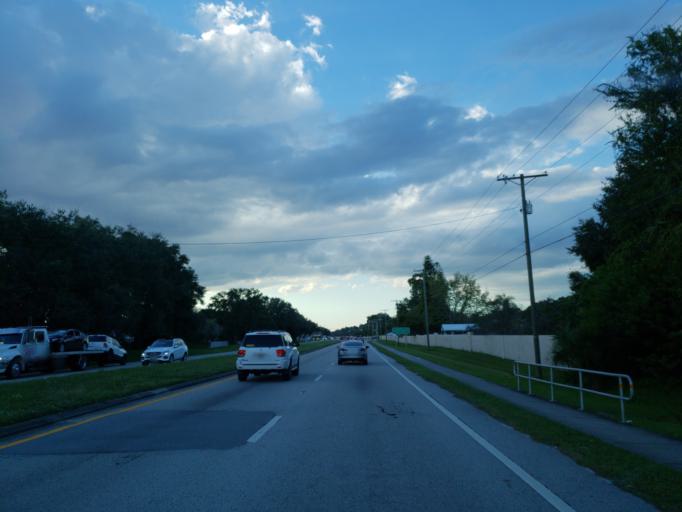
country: US
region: Florida
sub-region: Hillsborough County
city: Carrollwood Village
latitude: 28.0502
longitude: -82.5209
